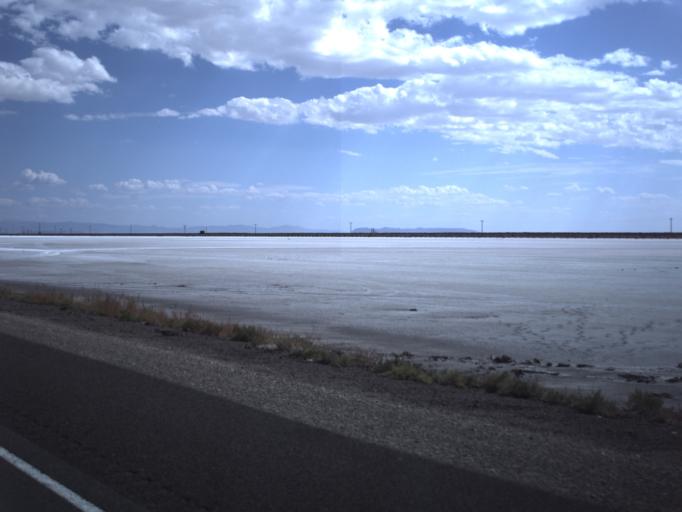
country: US
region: Utah
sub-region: Tooele County
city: Wendover
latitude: 40.7348
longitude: -113.6744
